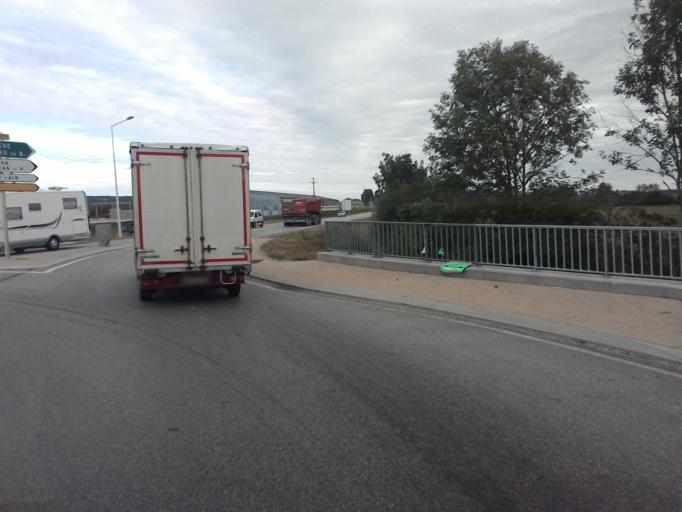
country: FR
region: Rhone-Alpes
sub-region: Departement de l'Ain
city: Ambronay
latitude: 46.0098
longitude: 5.3410
